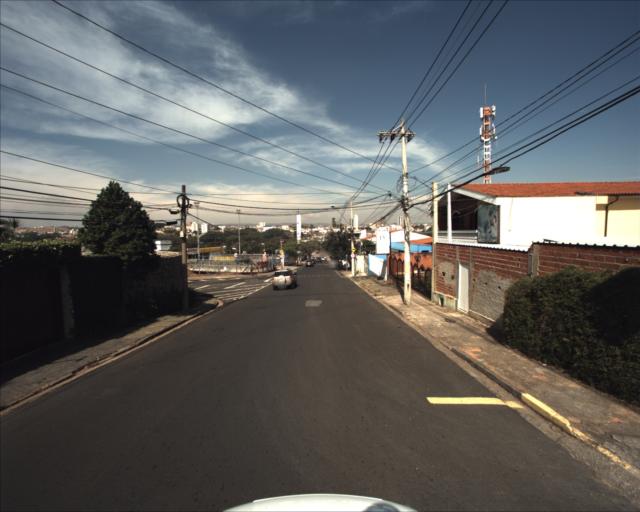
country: BR
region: Sao Paulo
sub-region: Sorocaba
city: Sorocaba
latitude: -23.4901
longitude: -47.4470
